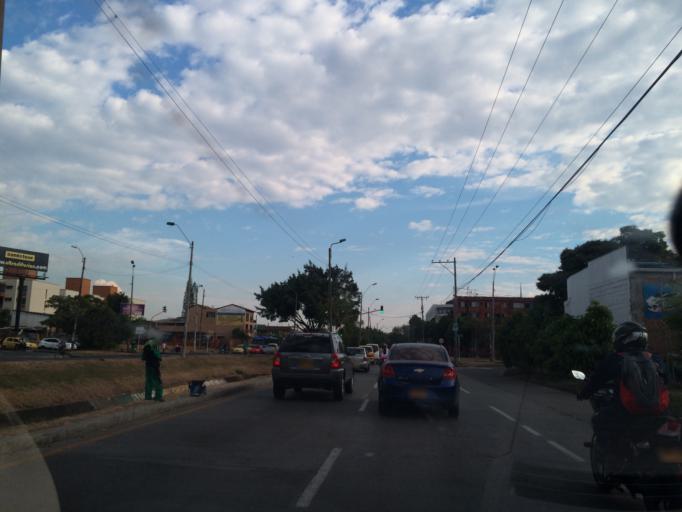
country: CO
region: Valle del Cauca
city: Cali
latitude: 3.4060
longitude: -76.5355
